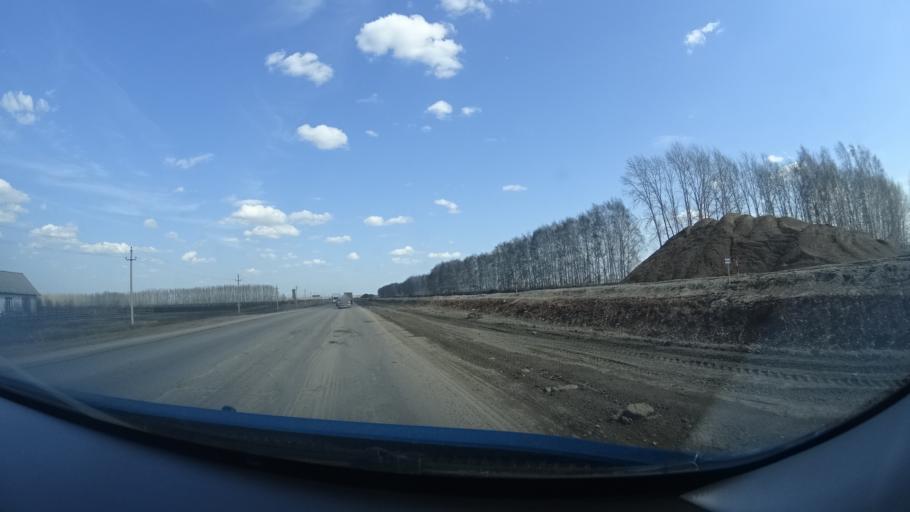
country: RU
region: Bashkortostan
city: Buzdyak
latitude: 54.6483
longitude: 54.5845
